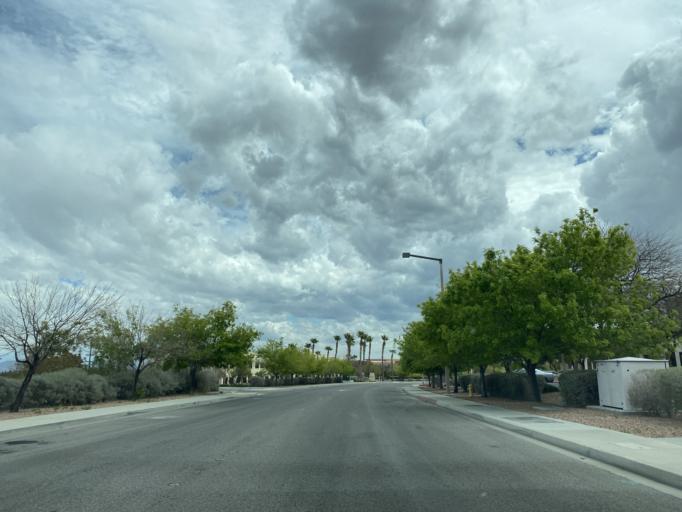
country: US
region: Nevada
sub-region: Clark County
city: Summerlin South
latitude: 36.1887
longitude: -115.3126
